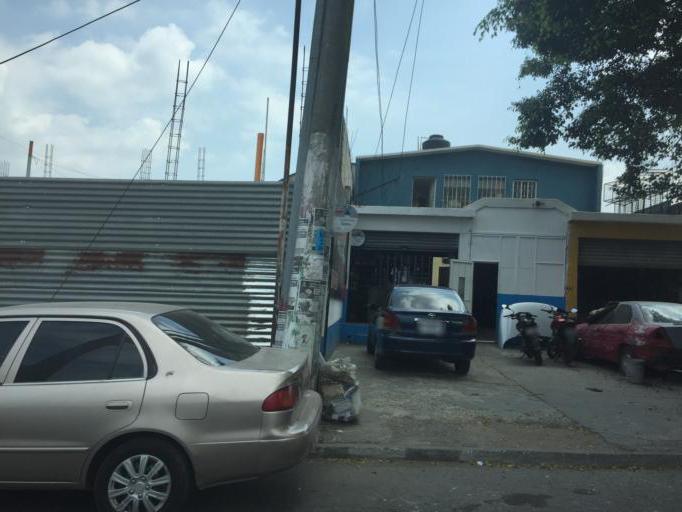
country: GT
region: Guatemala
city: Petapa
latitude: 14.5279
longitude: -90.5540
